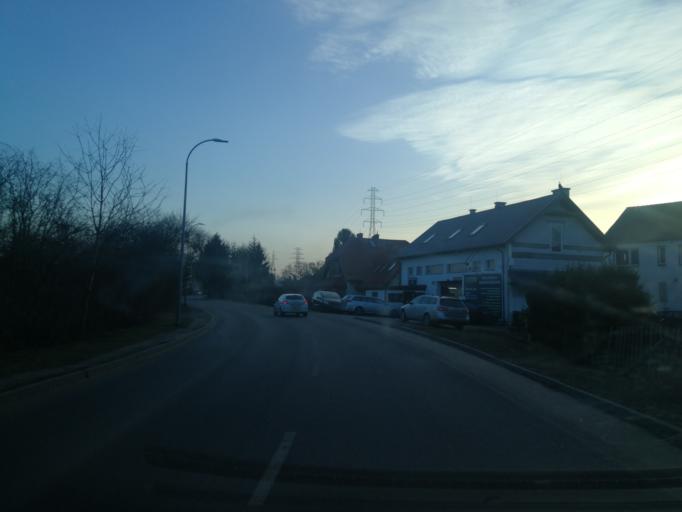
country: PL
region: Pomeranian Voivodeship
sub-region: Gdansk
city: Gdansk
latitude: 54.3913
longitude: 18.6338
